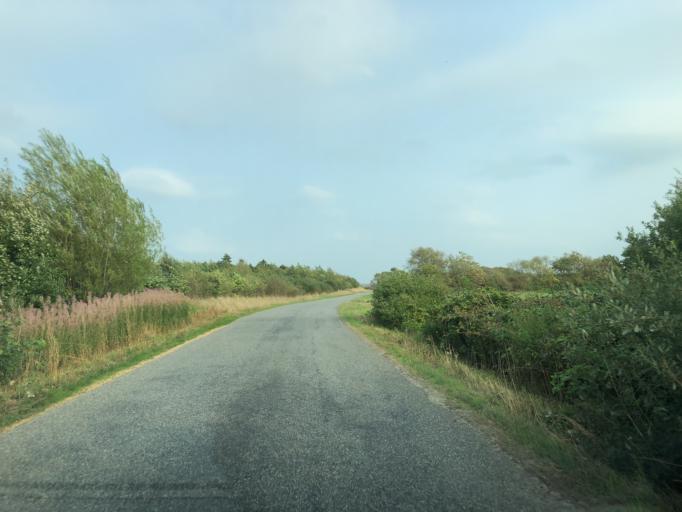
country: DK
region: Central Jutland
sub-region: Ringkobing-Skjern Kommune
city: Videbaek
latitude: 56.1196
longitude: 8.6801
